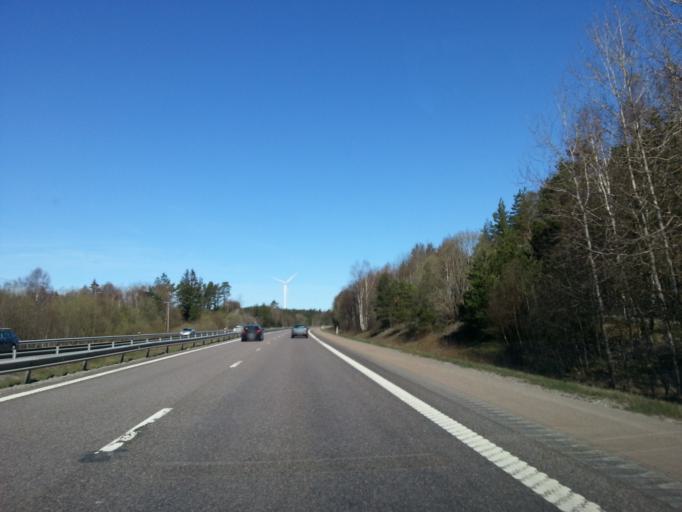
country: SE
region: Vaestra Goetaland
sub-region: Kungalvs Kommun
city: Kode
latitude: 57.9139
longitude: 11.8899
